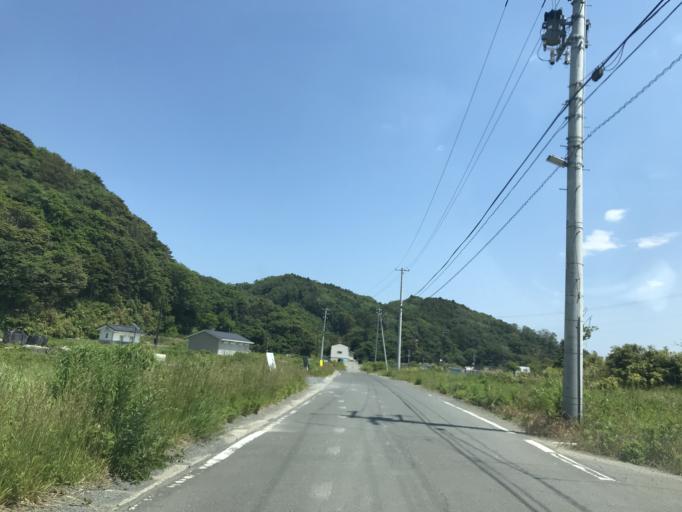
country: JP
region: Miyagi
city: Yamoto
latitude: 38.3293
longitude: 141.1636
